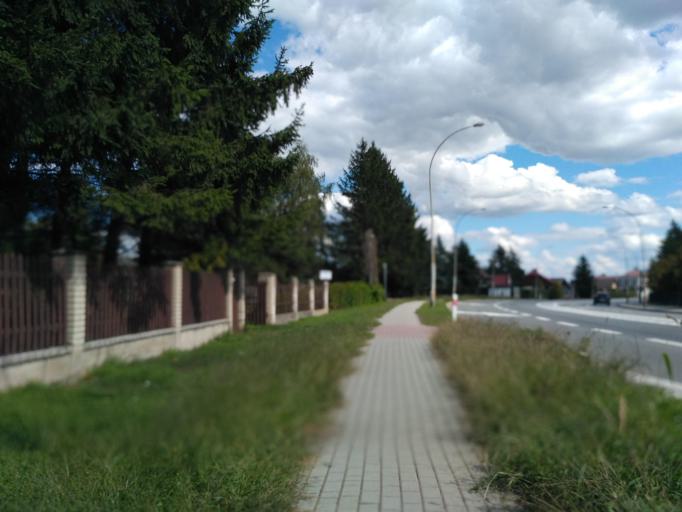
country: PL
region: Subcarpathian Voivodeship
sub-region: Powiat jasielski
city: Jaslo
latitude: 49.7569
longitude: 21.4966
